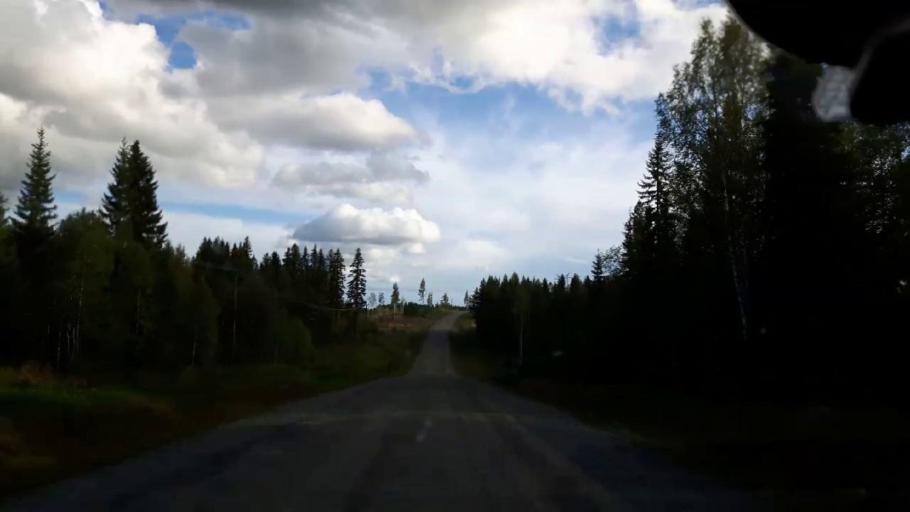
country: SE
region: Jaemtland
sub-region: Stroemsunds Kommun
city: Stroemsund
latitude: 63.3126
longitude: 15.5899
